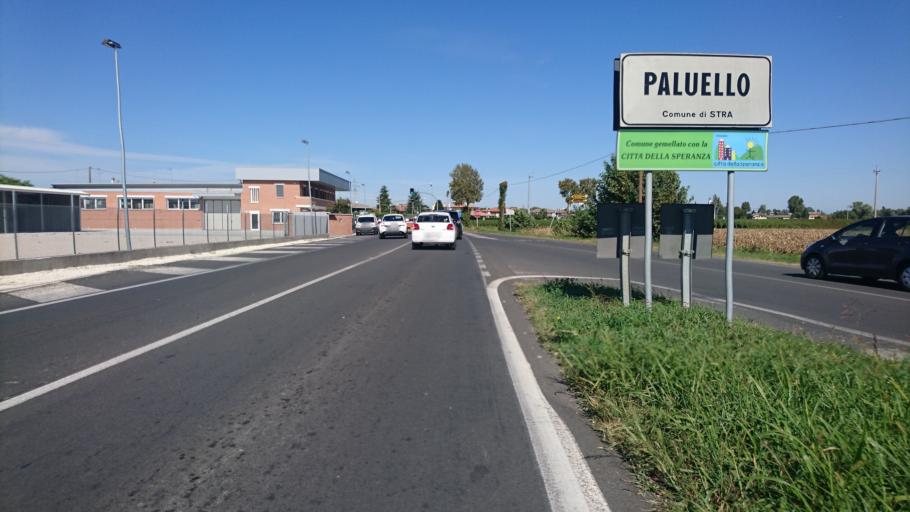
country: IT
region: Veneto
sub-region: Provincia di Venezia
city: Fosso
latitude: 45.4052
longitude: 12.0513
